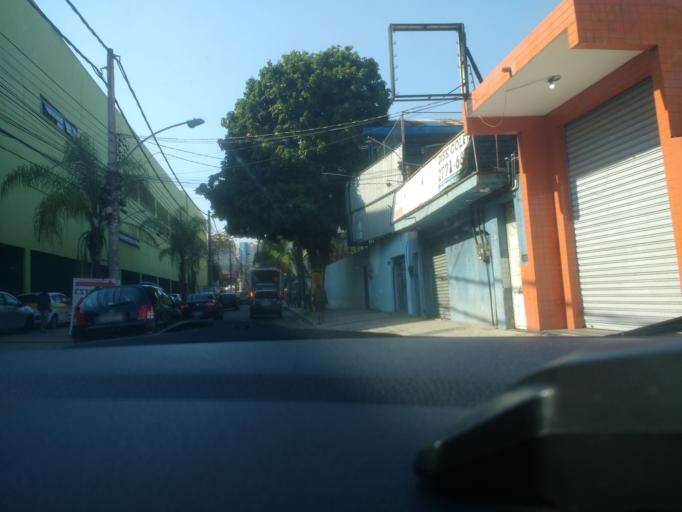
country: BR
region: Rio de Janeiro
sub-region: Duque De Caxias
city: Duque de Caxias
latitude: -22.7934
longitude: -43.3012
